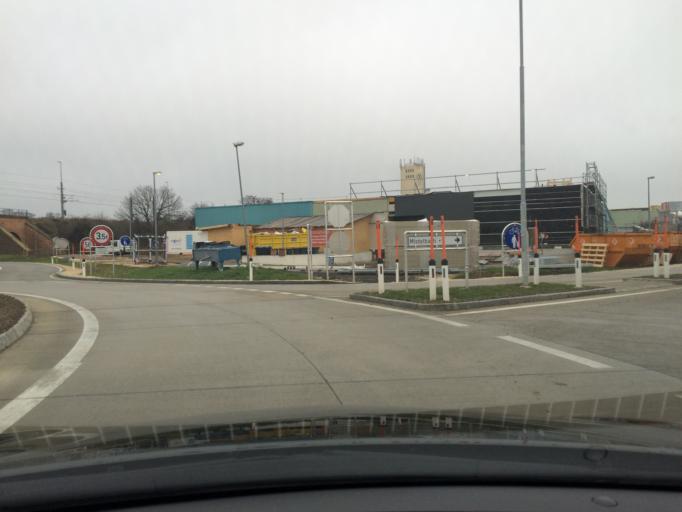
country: AT
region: Lower Austria
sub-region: Politischer Bezirk Mistelbach
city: Mistelbach
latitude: 48.5615
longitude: 16.5552
